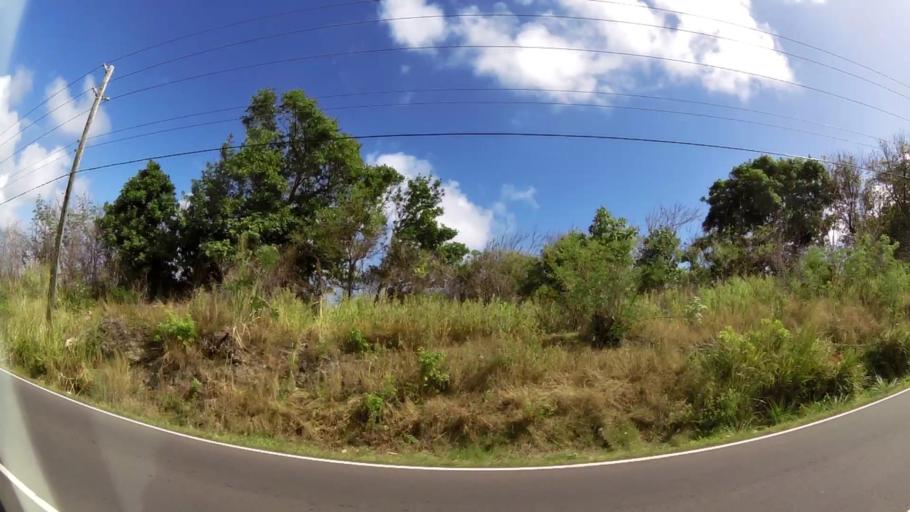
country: LC
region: Micoud Quarter
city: Micoud
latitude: 13.8039
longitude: -60.9035
